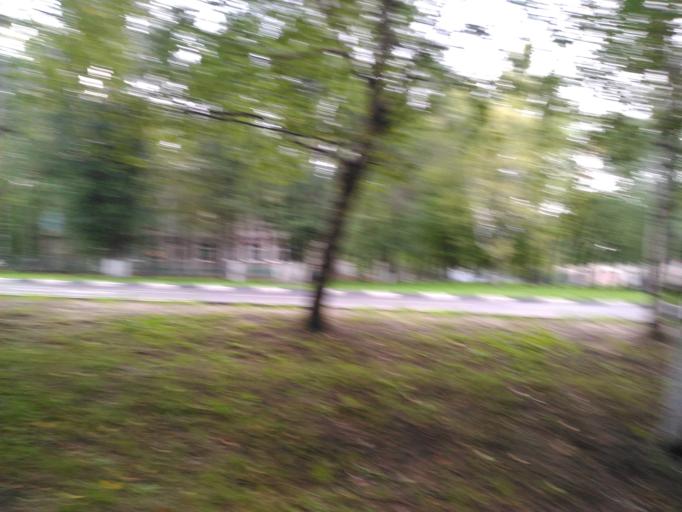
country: RU
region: Ulyanovsk
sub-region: Ulyanovskiy Rayon
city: Ulyanovsk
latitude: 54.2694
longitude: 48.3350
